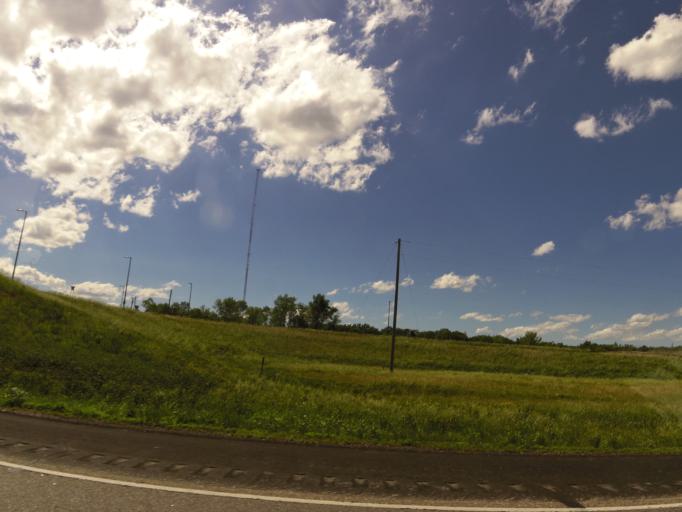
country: US
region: Minnesota
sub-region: Stearns County
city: Waite Park
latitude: 45.5159
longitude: -94.2264
